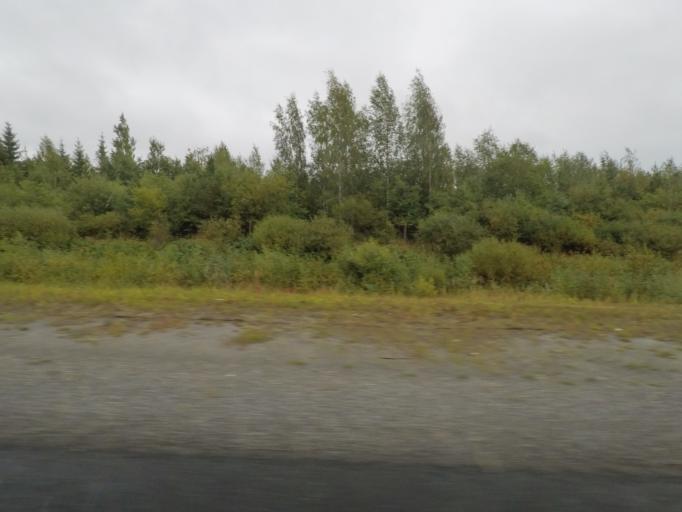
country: FI
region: Northern Savo
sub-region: Kuopio
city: Kuopio
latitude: 62.7562
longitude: 27.5804
